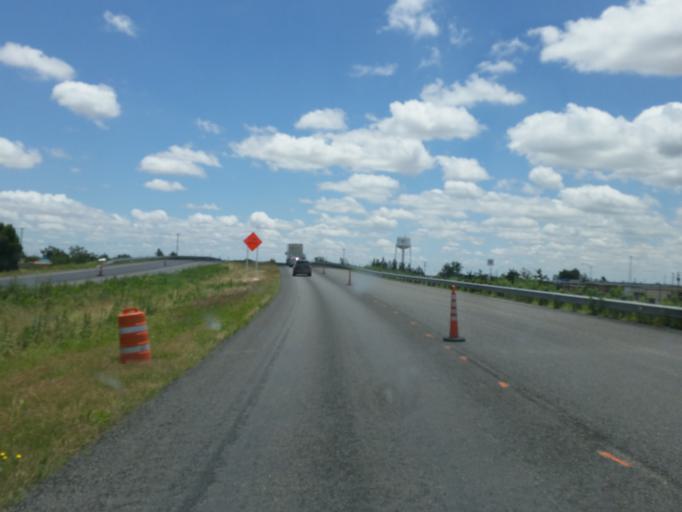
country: US
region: Texas
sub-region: Scurry County
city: Snyder
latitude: 32.7408
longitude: -100.9206
